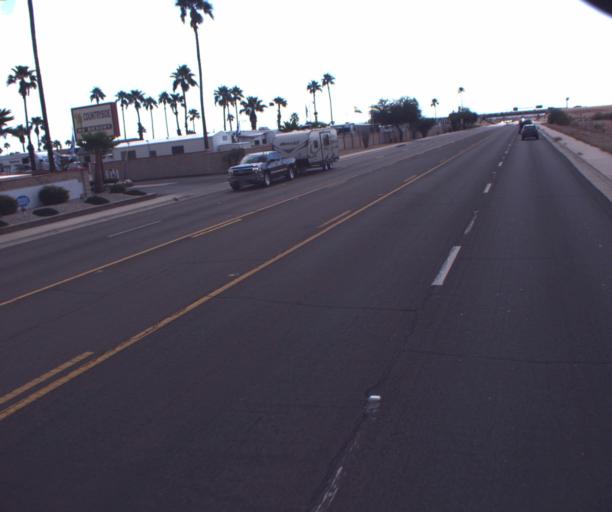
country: US
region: Arizona
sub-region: Pinal County
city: Apache Junction
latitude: 33.3909
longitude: -111.5461
